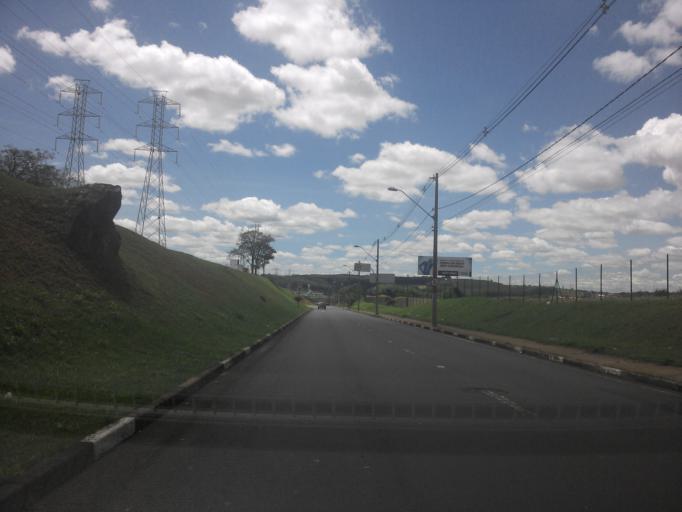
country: BR
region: Sao Paulo
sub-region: Campinas
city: Campinas
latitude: -22.8941
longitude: -47.0240
